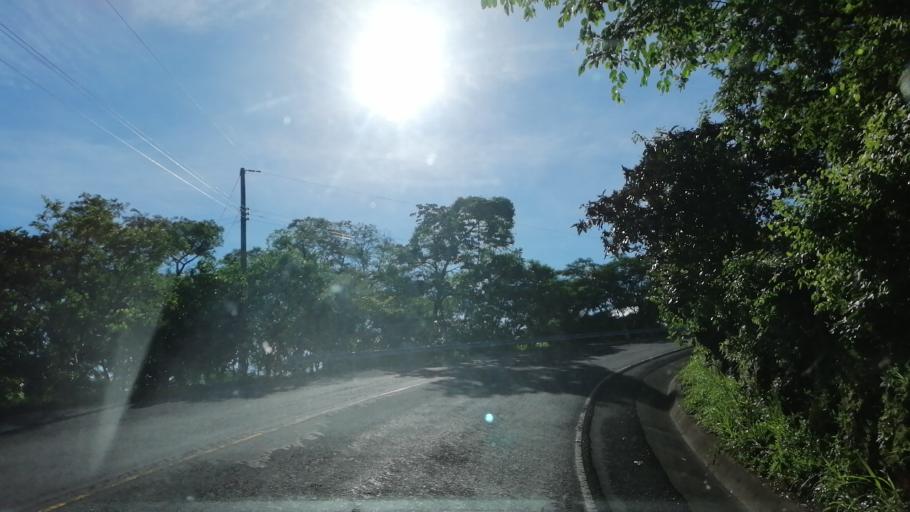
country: SV
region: Morazan
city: Cacaopera
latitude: 13.7930
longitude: -88.1233
